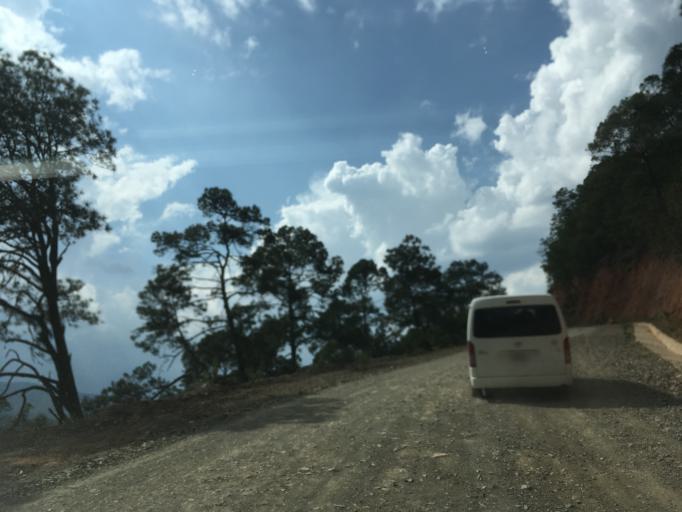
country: MX
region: Oaxaca
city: Santiago Tilantongo
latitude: 17.2008
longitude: -97.2800
